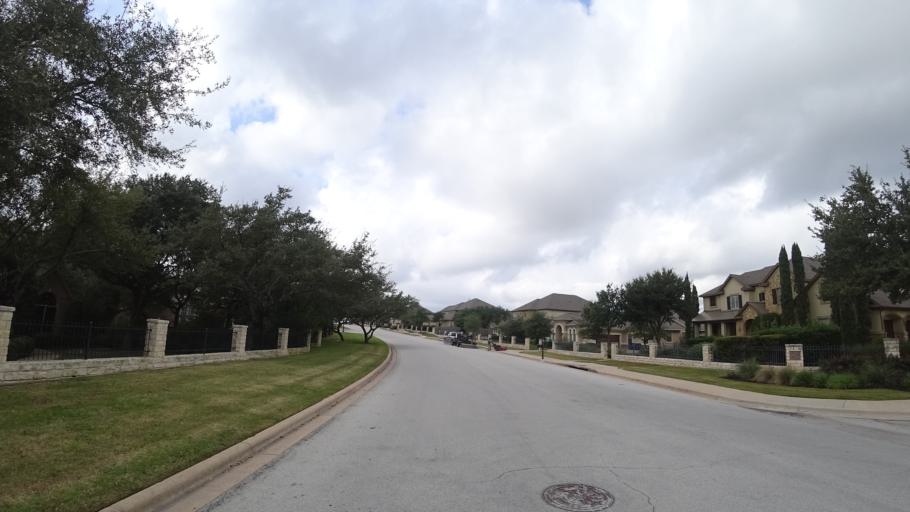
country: US
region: Texas
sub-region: Travis County
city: Barton Creek
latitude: 30.3124
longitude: -97.8999
